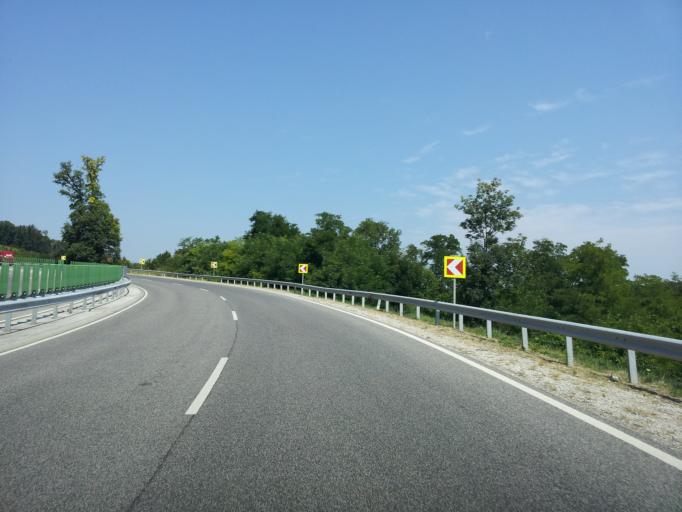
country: HU
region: Zala
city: Pacsa
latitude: 46.8289
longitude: 16.9719
